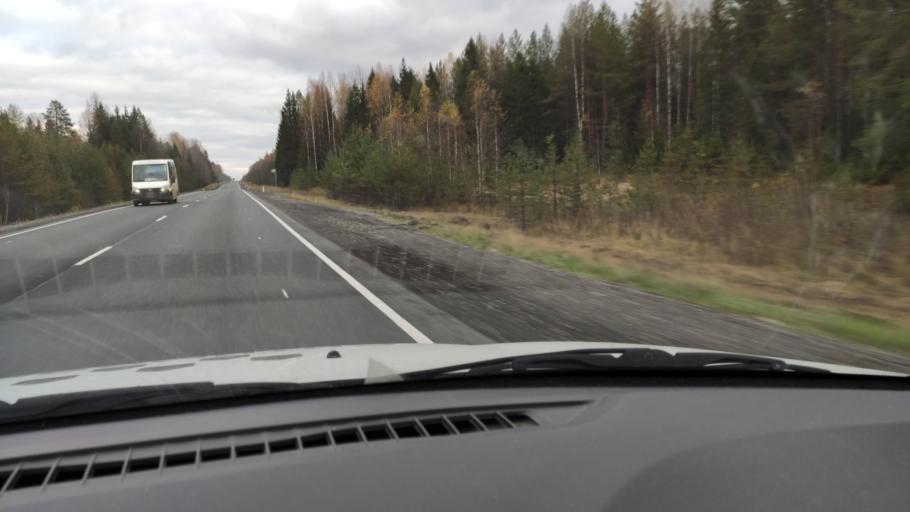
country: RU
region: Kirov
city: Chernaya Kholunitsa
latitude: 58.8873
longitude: 51.3810
